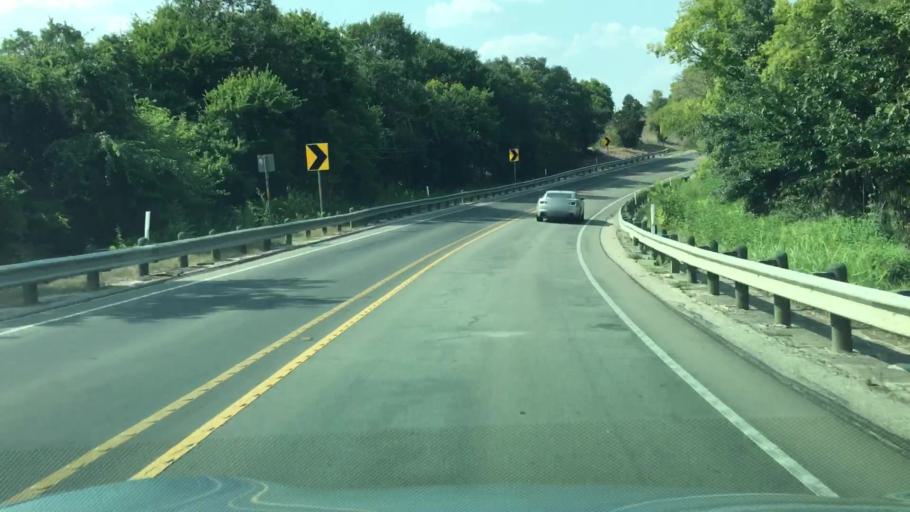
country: US
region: Texas
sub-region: Hays County
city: Dripping Springs
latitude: 30.1490
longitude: -98.0915
